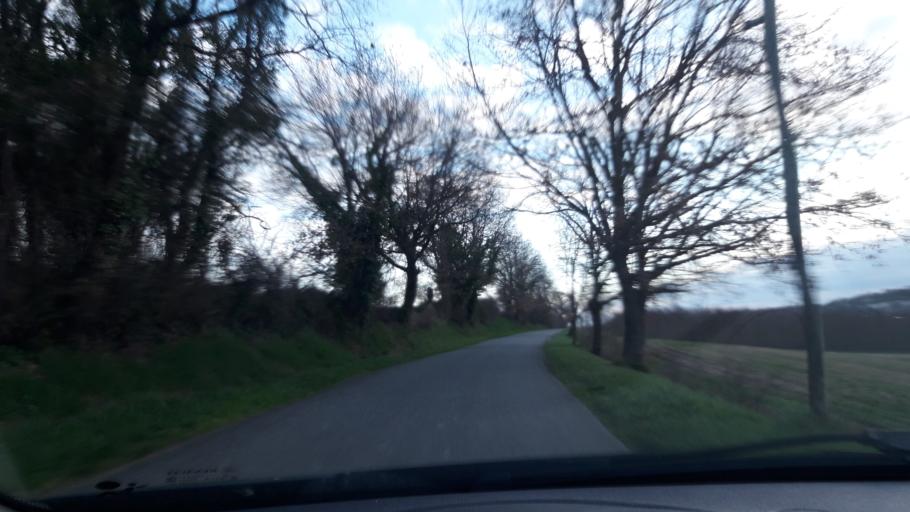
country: FR
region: Midi-Pyrenees
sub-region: Departement de la Haute-Garonne
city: Levignac
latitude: 43.6641
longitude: 1.1737
